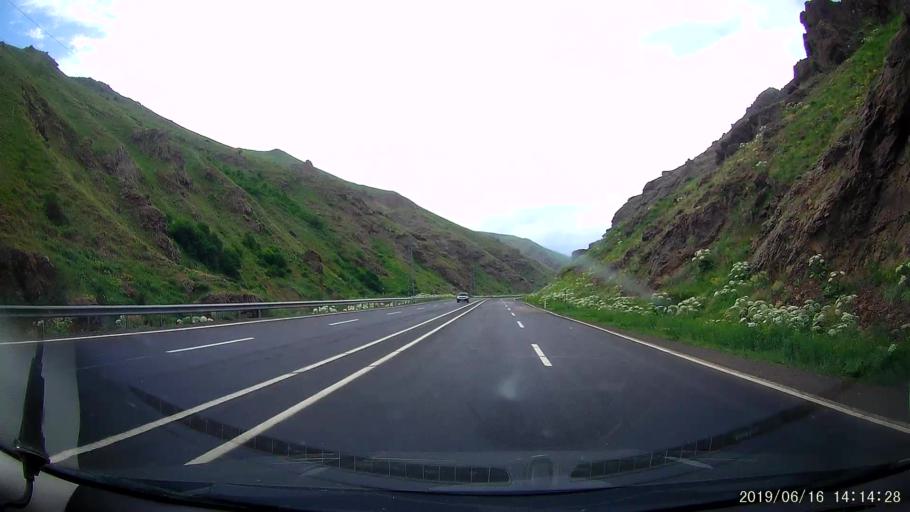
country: TR
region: Agri
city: Tahir
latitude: 39.7958
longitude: 42.4969
